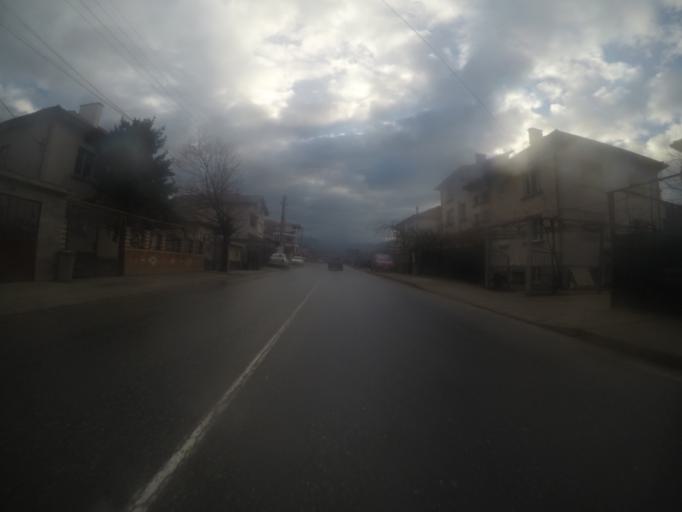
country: BG
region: Blagoevgrad
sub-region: Obshtina Simitli
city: Simitli
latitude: 41.8815
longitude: 23.1228
